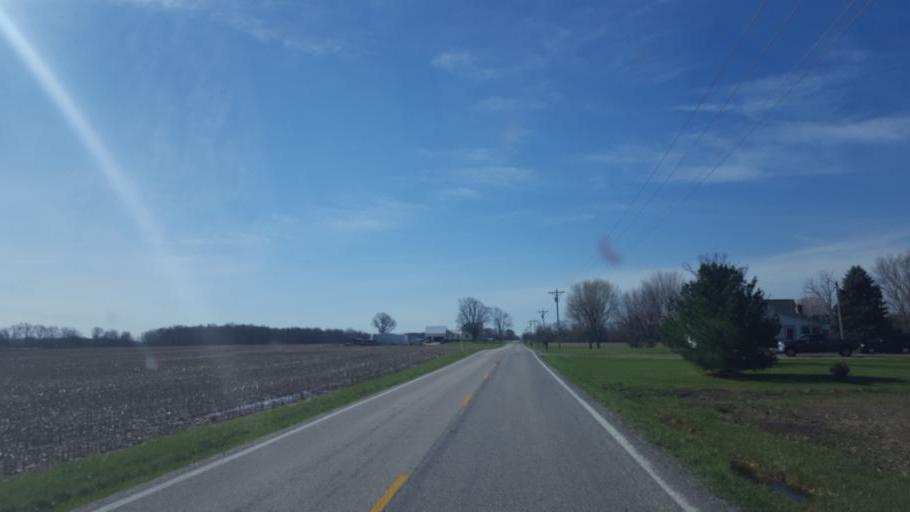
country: US
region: Ohio
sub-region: Morrow County
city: Cardington
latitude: 40.5711
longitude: -82.9622
